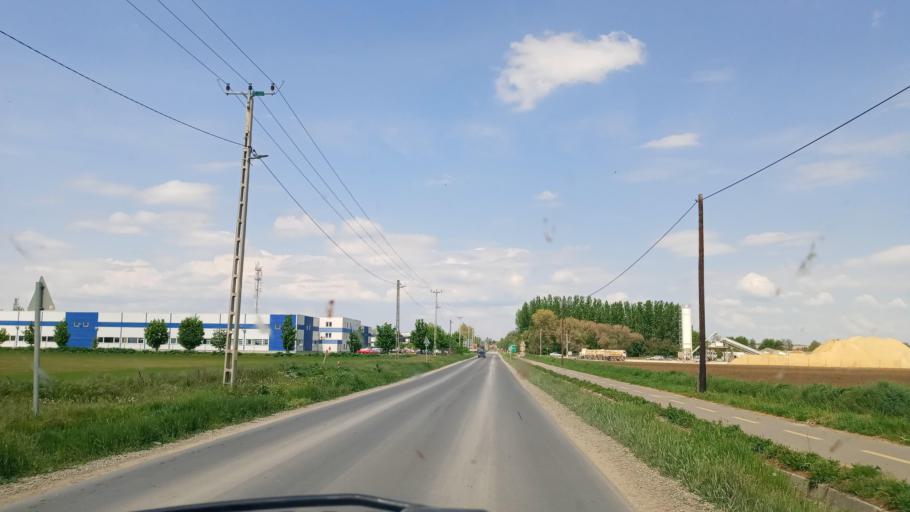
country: HU
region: Baranya
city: Boly
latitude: 45.9543
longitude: 18.5302
